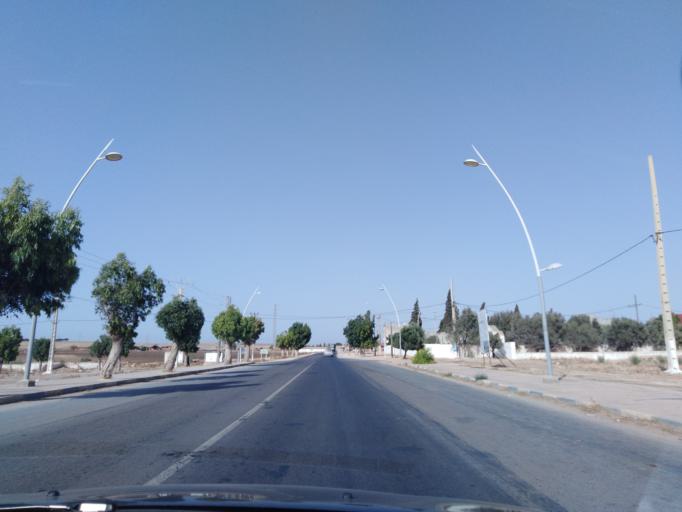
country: MA
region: Doukkala-Abda
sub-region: Safi
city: Safi
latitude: 32.2579
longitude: -8.9727
